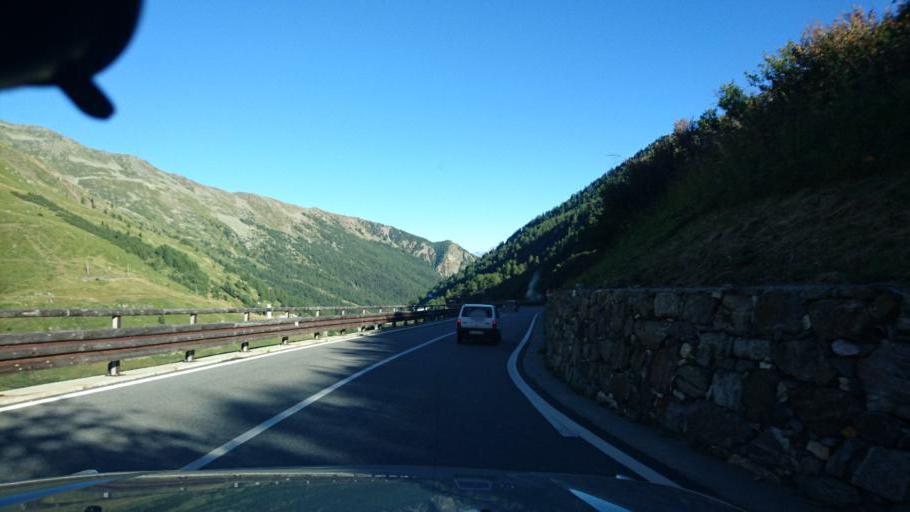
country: IT
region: Aosta Valley
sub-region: Valle d'Aosta
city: San Leonardo
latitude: 45.8541
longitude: 7.1513
